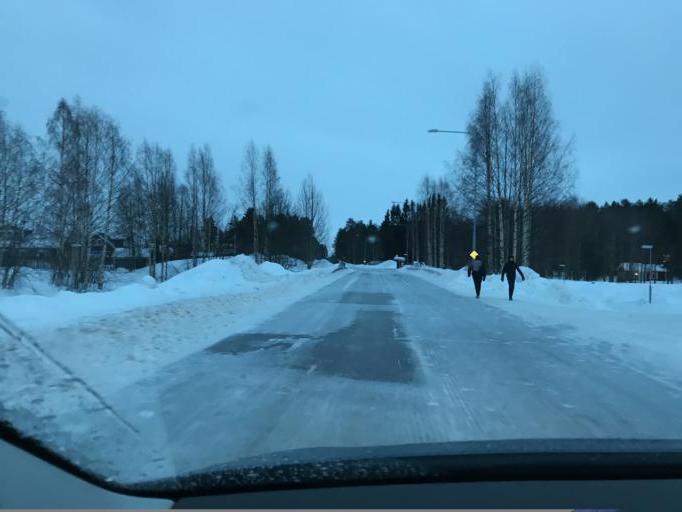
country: SE
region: Norrbotten
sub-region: Lulea Kommun
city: Sodra Sunderbyn
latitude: 65.6541
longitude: 21.9473
